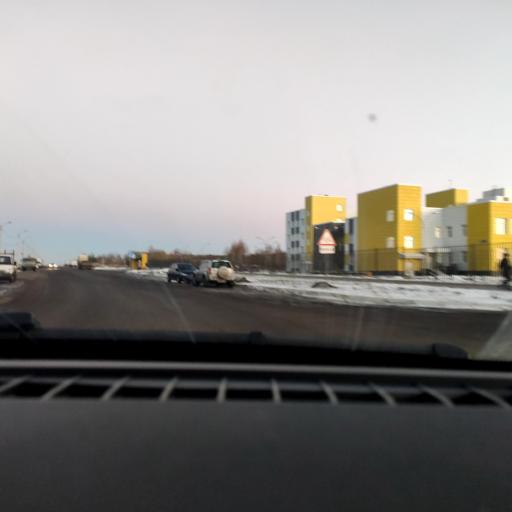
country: RU
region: Voronezj
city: Maslovka
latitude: 51.6329
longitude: 39.2927
